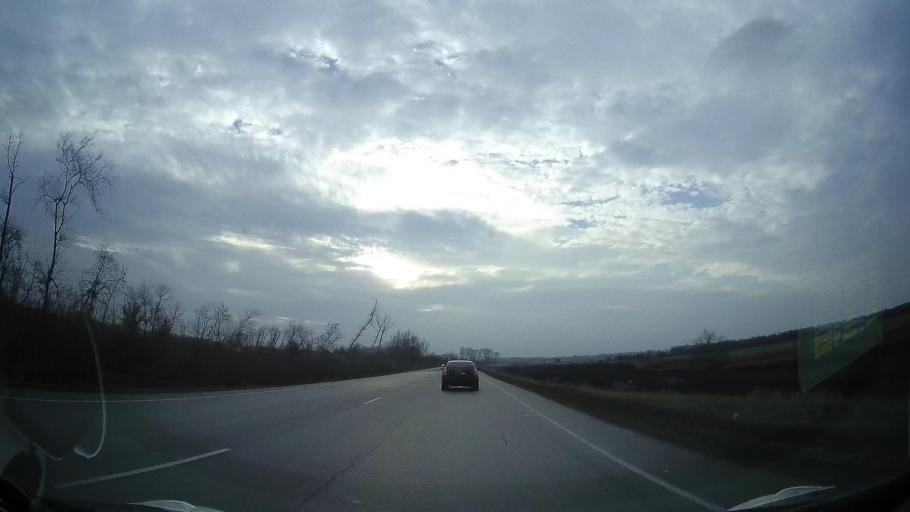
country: RU
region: Rostov
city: Ol'ginskaya
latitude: 47.1338
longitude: 39.9831
